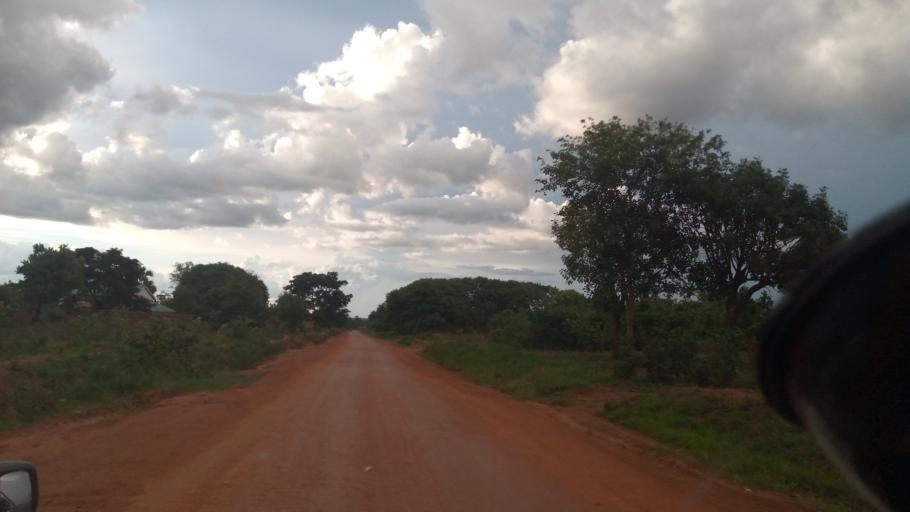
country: UG
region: Northern Region
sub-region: Lira District
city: Lira
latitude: 2.3730
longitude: 32.9350
